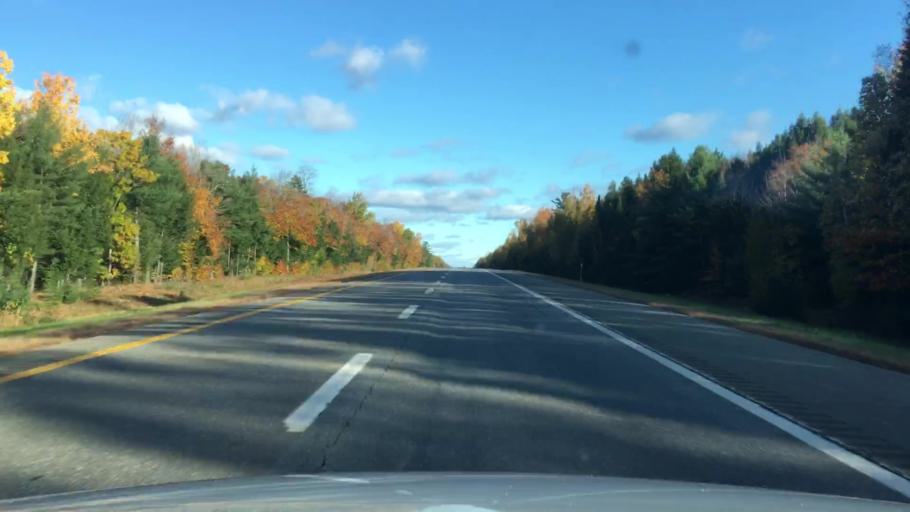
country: US
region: Maine
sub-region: Penobscot County
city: Greenbush
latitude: 45.0672
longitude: -68.6896
